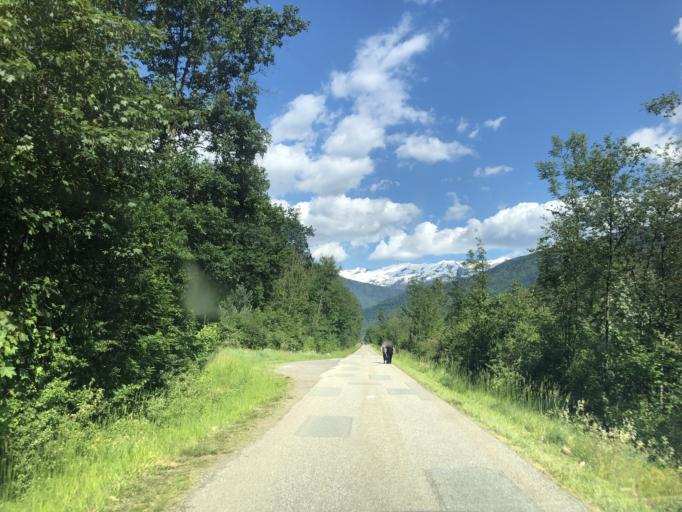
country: FR
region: Rhone-Alpes
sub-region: Departement de la Savoie
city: Aiton
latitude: 45.5617
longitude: 6.2123
